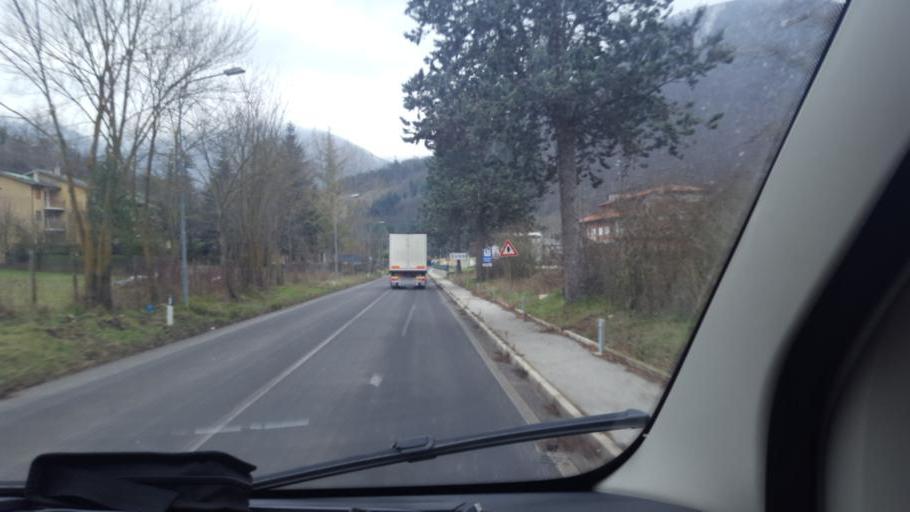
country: IT
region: The Marches
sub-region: Provincia di Macerata
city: Visso
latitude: 42.9366
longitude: 13.0820
